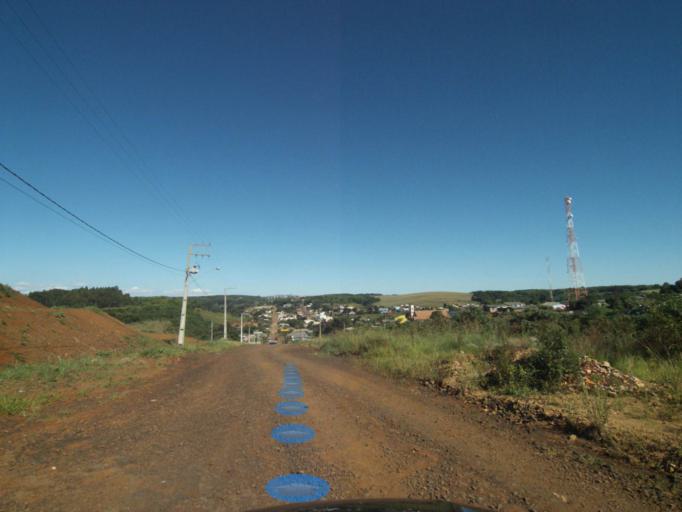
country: BR
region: Parana
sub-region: Coronel Vivida
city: Coronel Vivida
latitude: -26.1403
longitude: -52.3913
